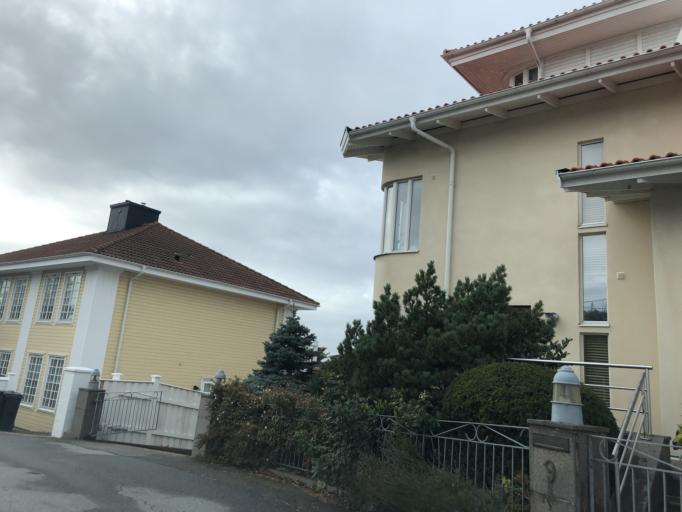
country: SE
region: Vaestra Goetaland
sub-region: Goteborg
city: Majorna
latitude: 57.6736
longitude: 11.8559
